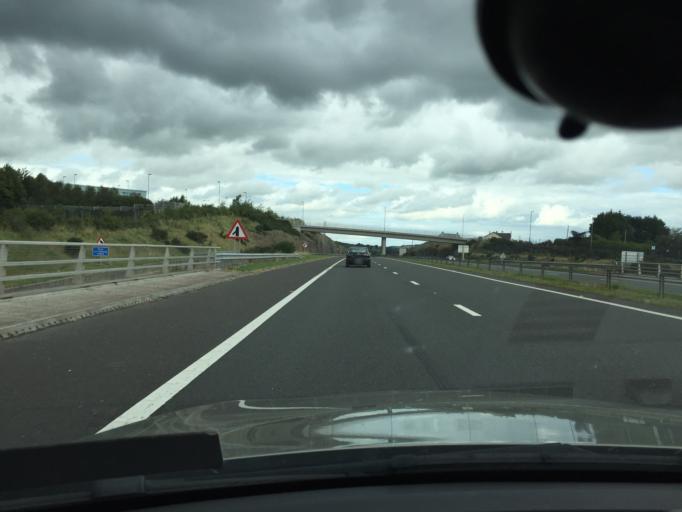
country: GB
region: Northern Ireland
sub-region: Newry and Mourne District
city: Newry
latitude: 54.1867
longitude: -6.3611
